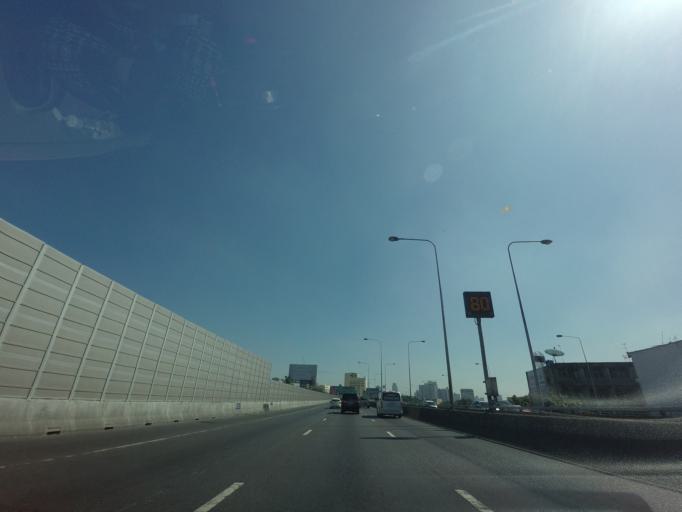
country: TH
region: Bangkok
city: Khlong Toei
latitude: 13.7128
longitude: 100.5706
